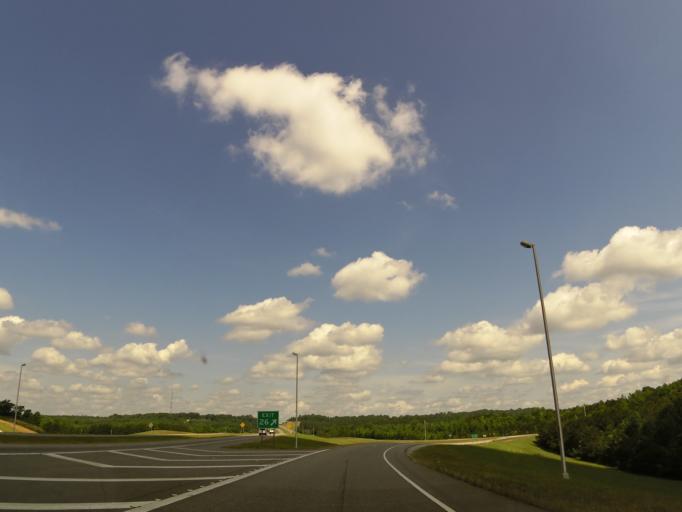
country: US
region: Alabama
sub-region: Marion County
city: Winfield
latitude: 34.0102
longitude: -87.8314
